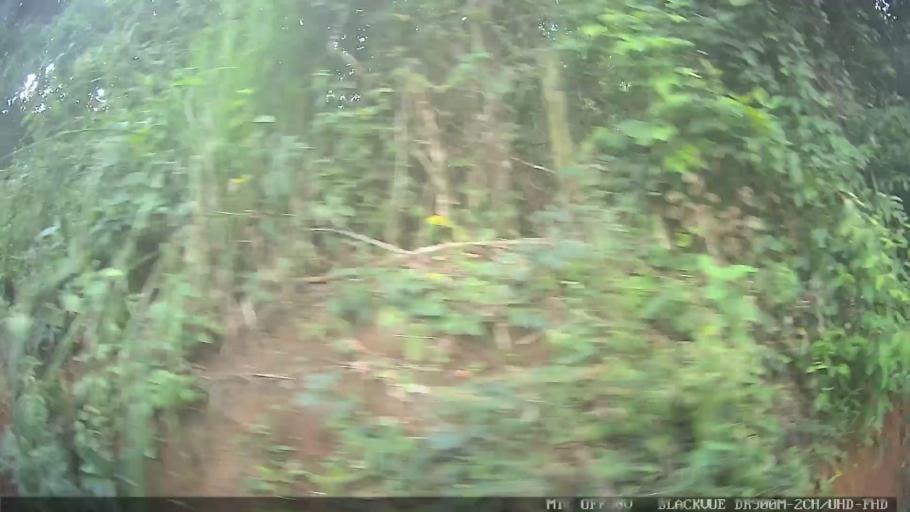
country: BR
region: Minas Gerais
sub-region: Extrema
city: Extrema
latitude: -22.8227
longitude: -46.2524
